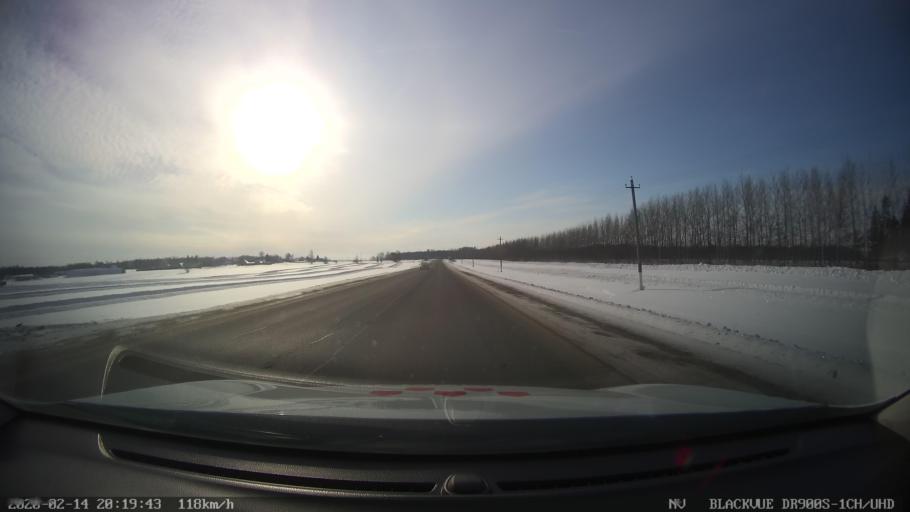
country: RU
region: Tatarstan
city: Verkhniy Uslon
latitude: 55.5666
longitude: 48.9014
